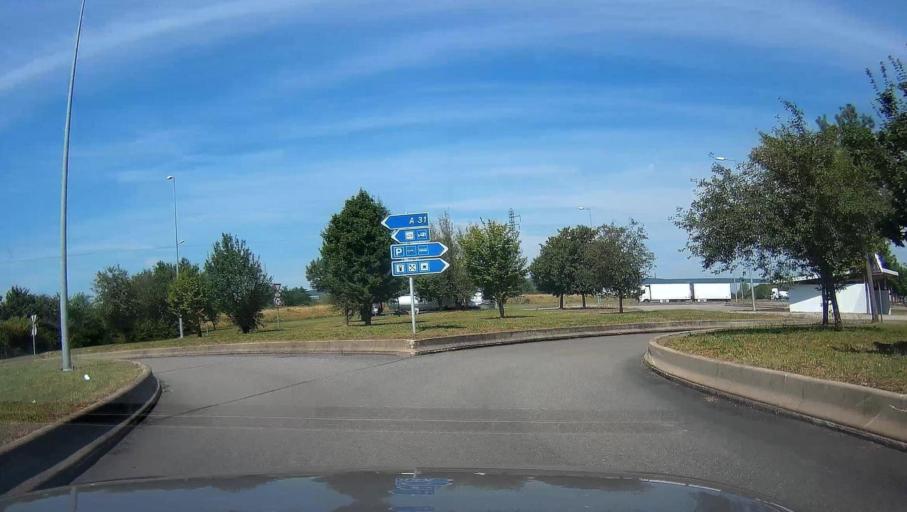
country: FR
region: Bourgogne
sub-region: Departement de la Cote-d'Or
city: Gevrey-Chambertin
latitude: 47.2174
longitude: 5.0012
